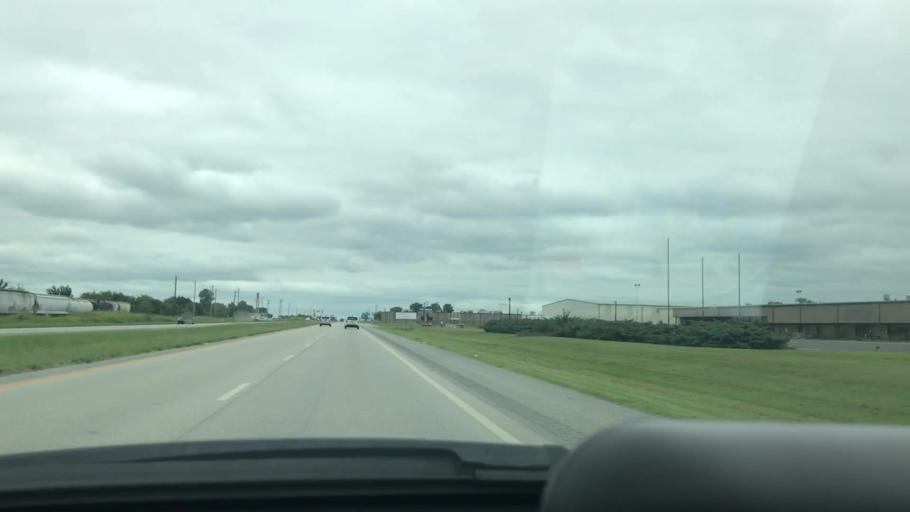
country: US
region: Oklahoma
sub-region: Mayes County
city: Chouteau
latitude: 36.2394
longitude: -95.3377
